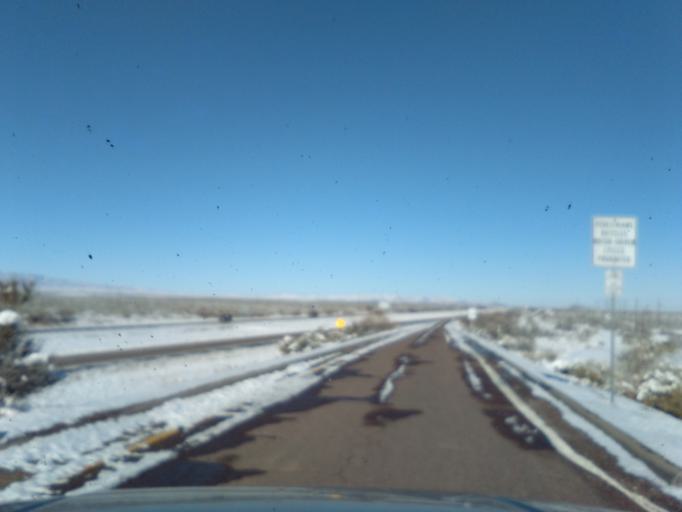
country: US
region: New Mexico
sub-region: Socorro County
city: Socorro
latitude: 33.6366
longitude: -107.1202
